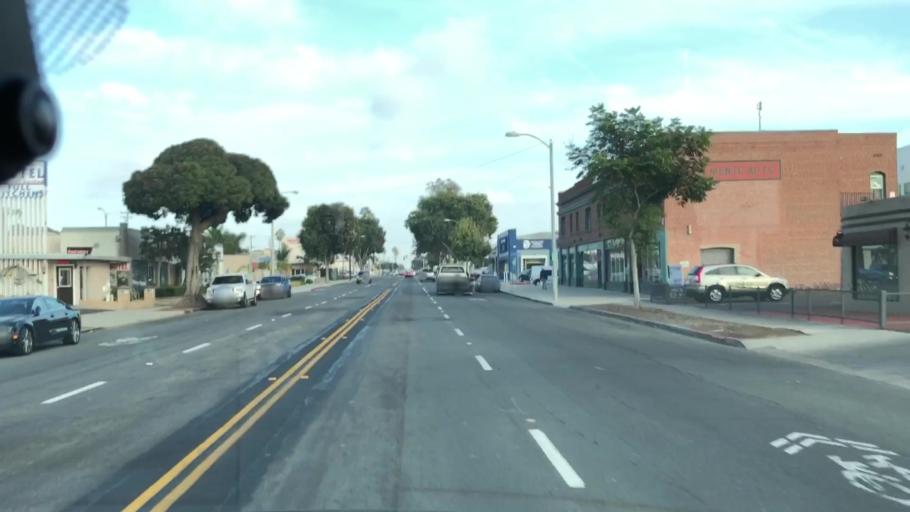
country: US
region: California
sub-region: Ventura County
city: Ventura
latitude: 34.2743
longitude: -119.2700
